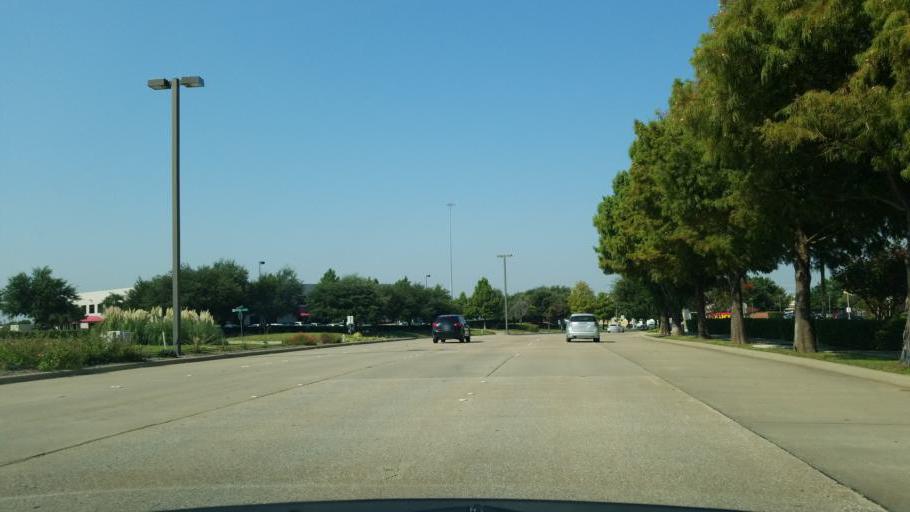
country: US
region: Texas
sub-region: Collin County
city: Allen
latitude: 33.0911
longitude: -96.6785
